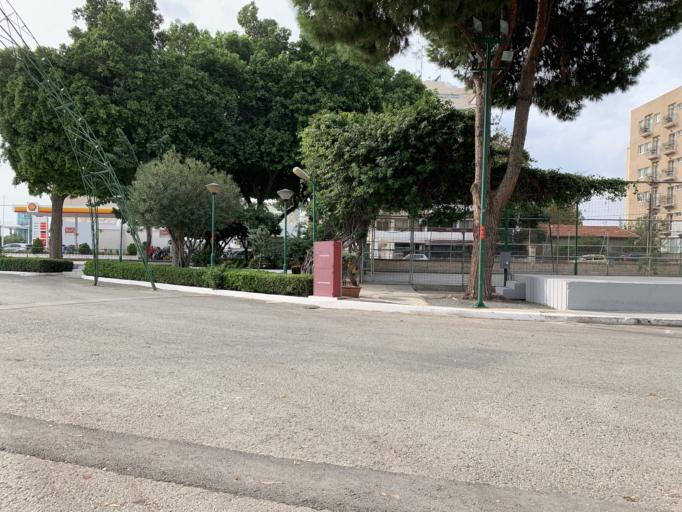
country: CY
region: Limassol
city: Limassol
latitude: 34.6820
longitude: 33.0551
